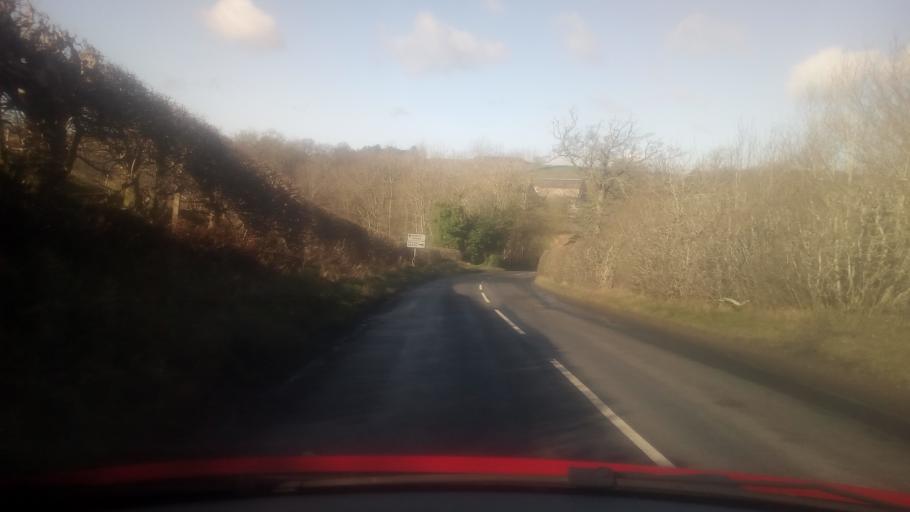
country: GB
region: Scotland
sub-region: The Scottish Borders
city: Melrose
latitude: 55.5271
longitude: -2.7301
